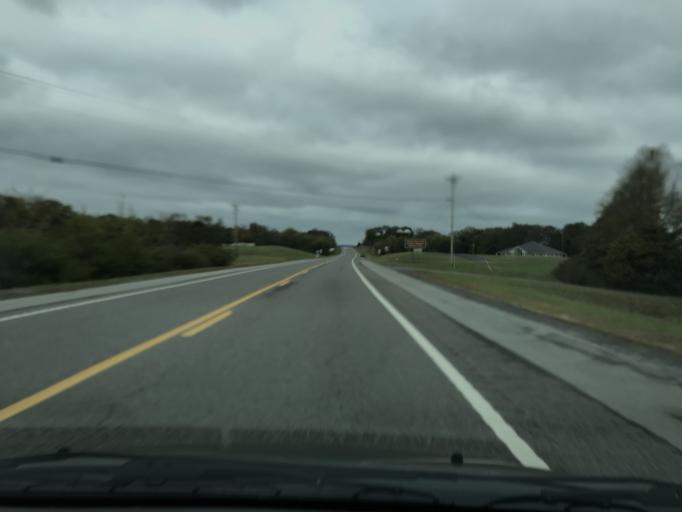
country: US
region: Tennessee
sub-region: Rhea County
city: Graysville
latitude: 35.3808
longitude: -85.0008
